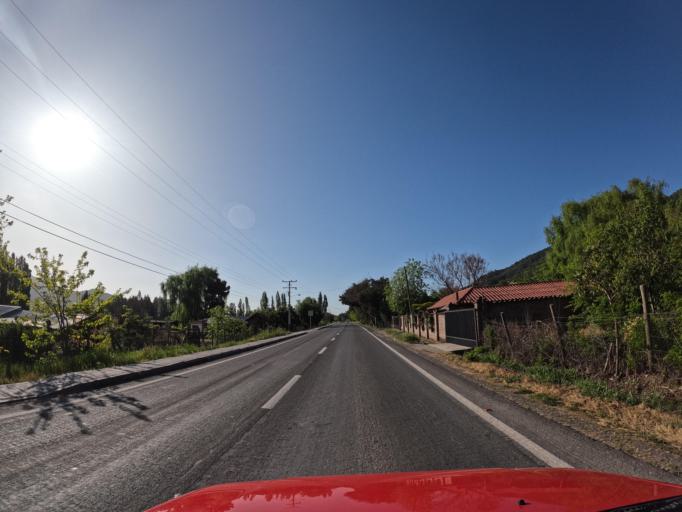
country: CL
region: Maule
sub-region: Provincia de Curico
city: Teno
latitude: -34.7959
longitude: -71.2259
